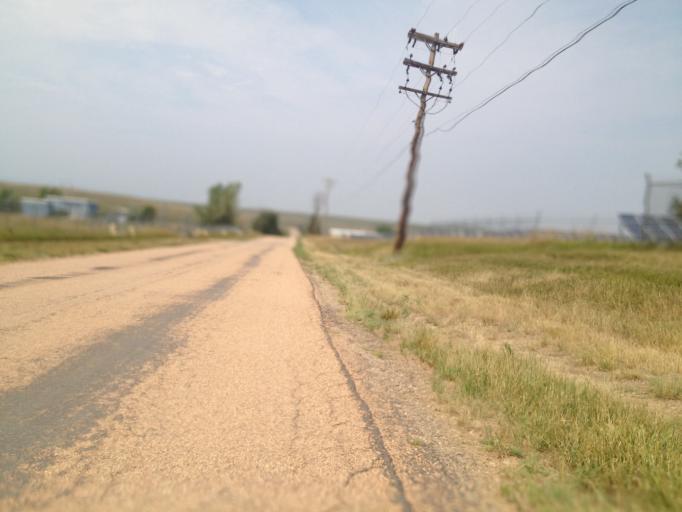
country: US
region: Colorado
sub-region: Boulder County
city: Superior
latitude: 39.9503
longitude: -105.1988
